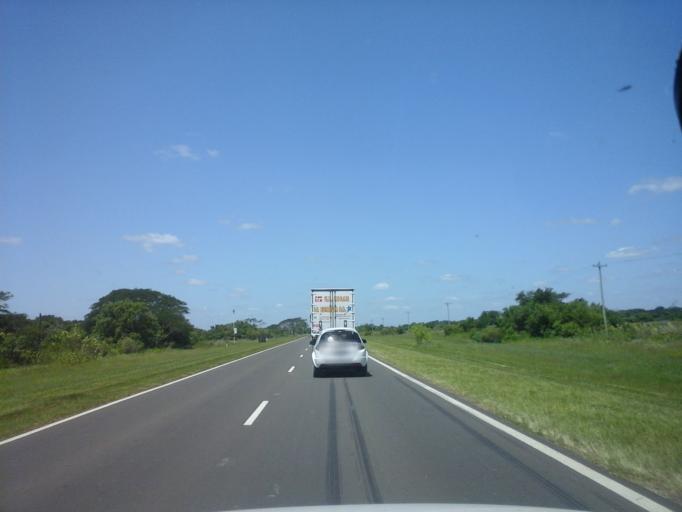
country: AR
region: Corrientes
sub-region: Departamento de Itati
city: Itati
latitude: -27.3412
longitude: -58.2159
